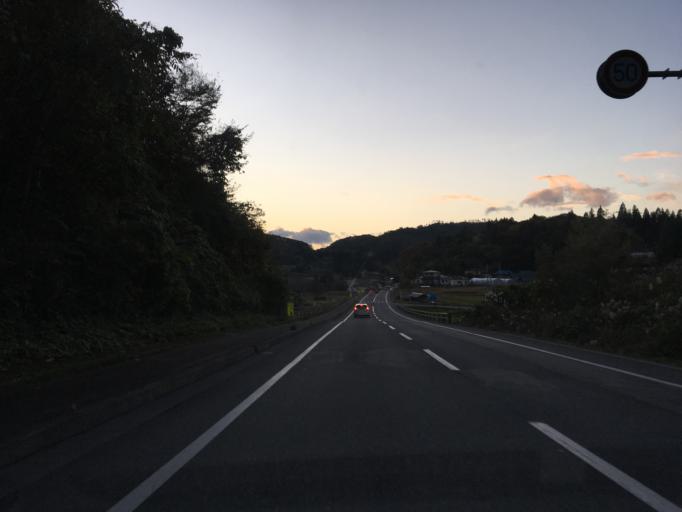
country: JP
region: Iwate
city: Kitakami
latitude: 39.2896
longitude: 141.2671
